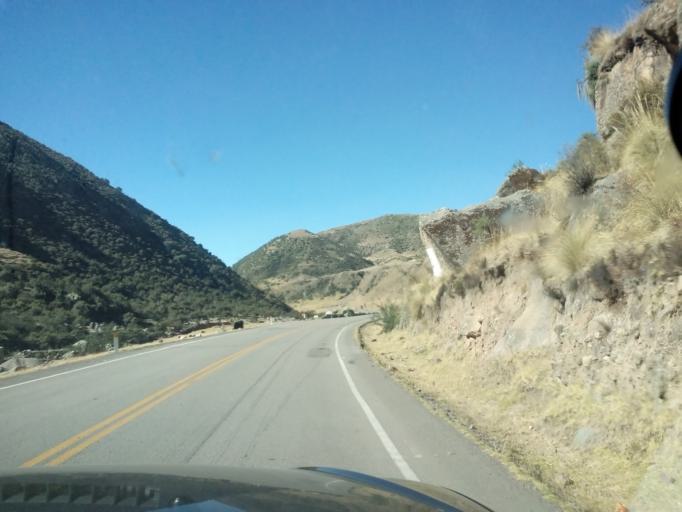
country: PE
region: Ayacucho
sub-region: Provincia de Huamanga
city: Vinchos
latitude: -13.3555
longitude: -74.4050
